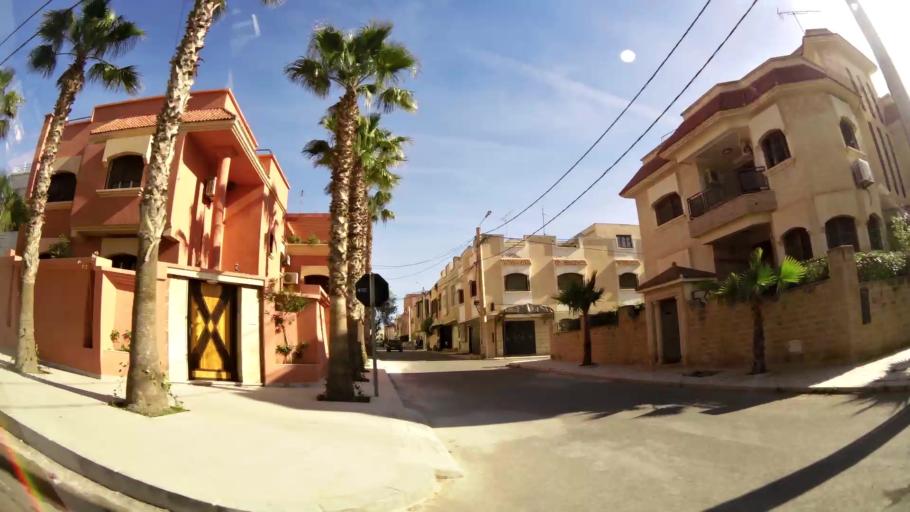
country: MA
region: Oriental
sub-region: Oujda-Angad
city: Oujda
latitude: 34.6631
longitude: -1.9005
